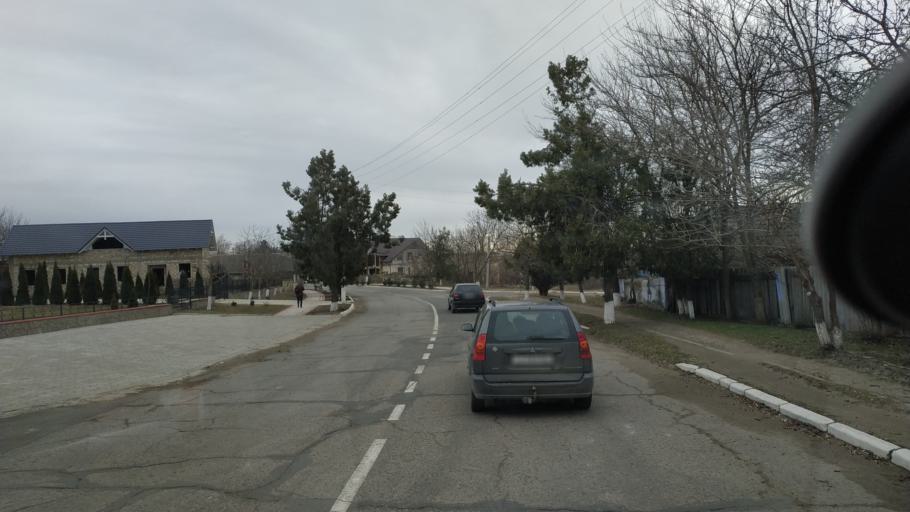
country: MD
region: Telenesti
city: Cocieri
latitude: 47.3088
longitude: 29.1083
